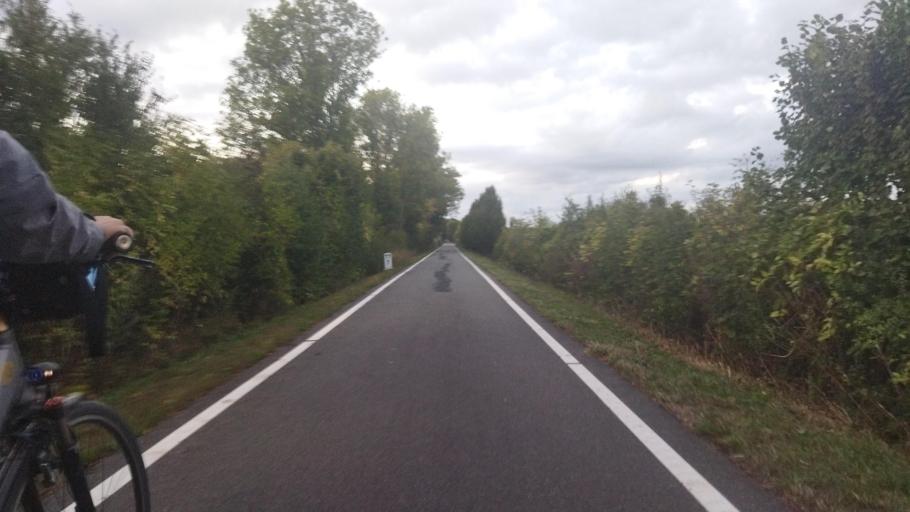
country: DE
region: North Rhine-Westphalia
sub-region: Regierungsbezirk Munster
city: Horstmar
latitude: 52.0706
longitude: 7.3207
